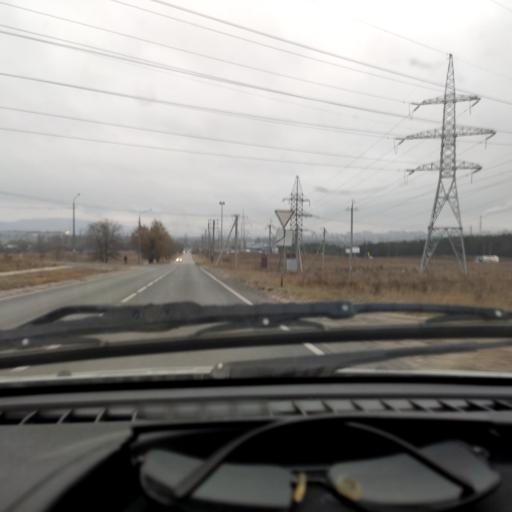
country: RU
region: Samara
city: Zhigulevsk
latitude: 53.4911
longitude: 49.5263
